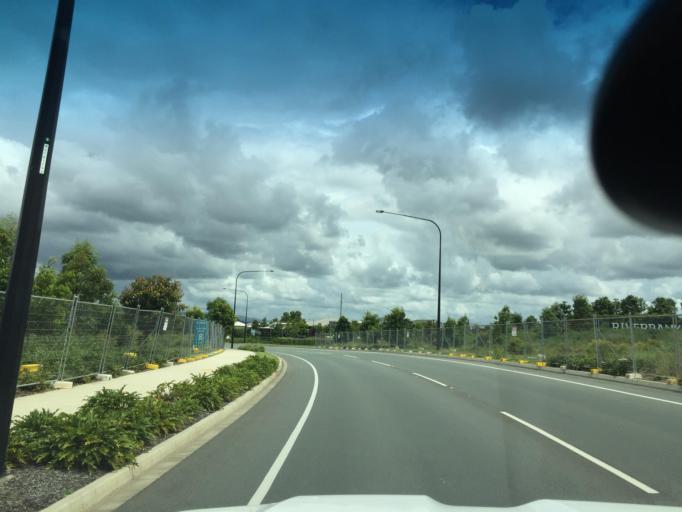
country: AU
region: Queensland
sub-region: Moreton Bay
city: Caboolture South
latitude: -27.0972
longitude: 152.9665
